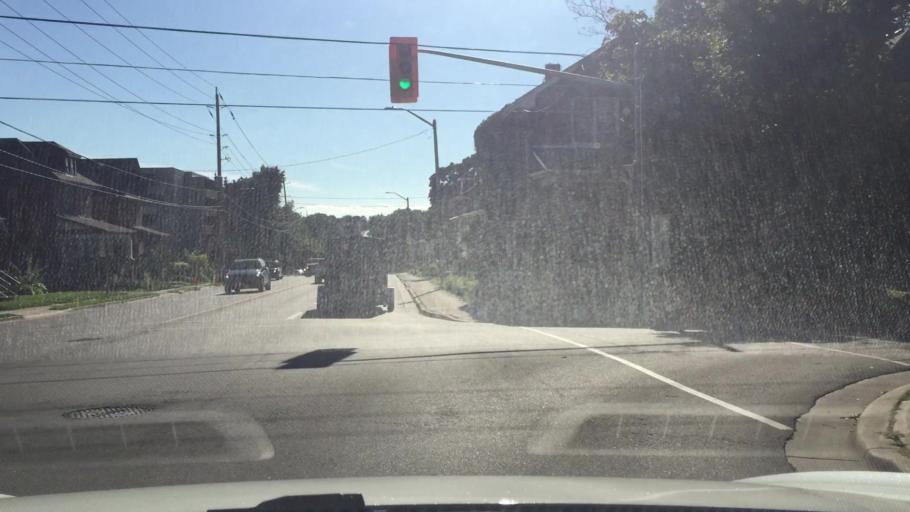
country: CA
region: Ontario
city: Oshawa
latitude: 43.9028
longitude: -78.8694
